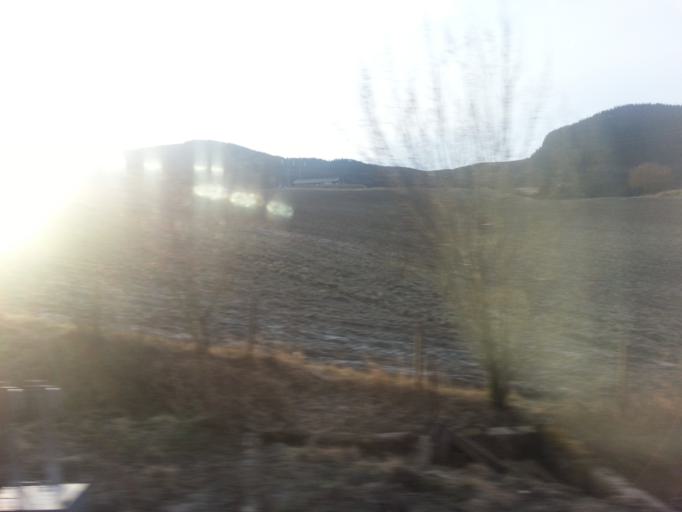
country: NO
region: Sor-Trondelag
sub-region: Melhus
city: Melhus
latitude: 63.3084
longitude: 10.3371
